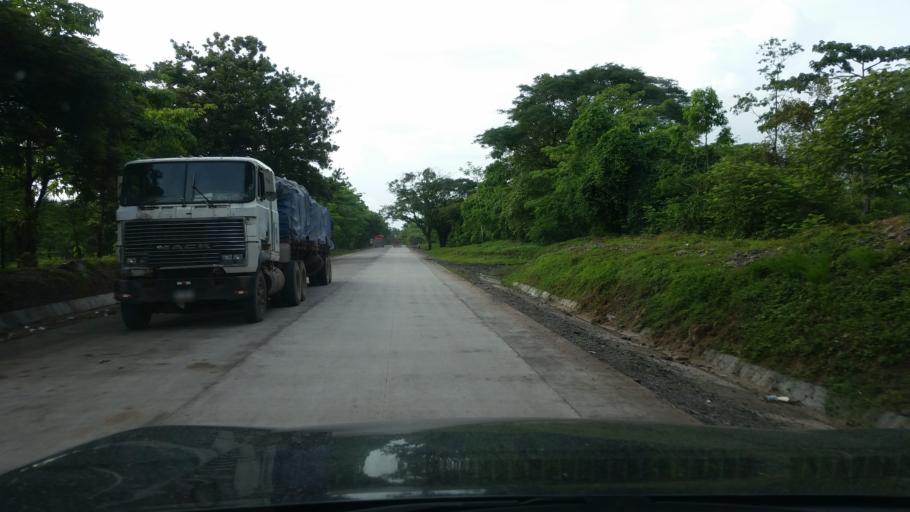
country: NI
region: Matagalpa
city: Rio Blanco
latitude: 13.0889
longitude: -85.0623
